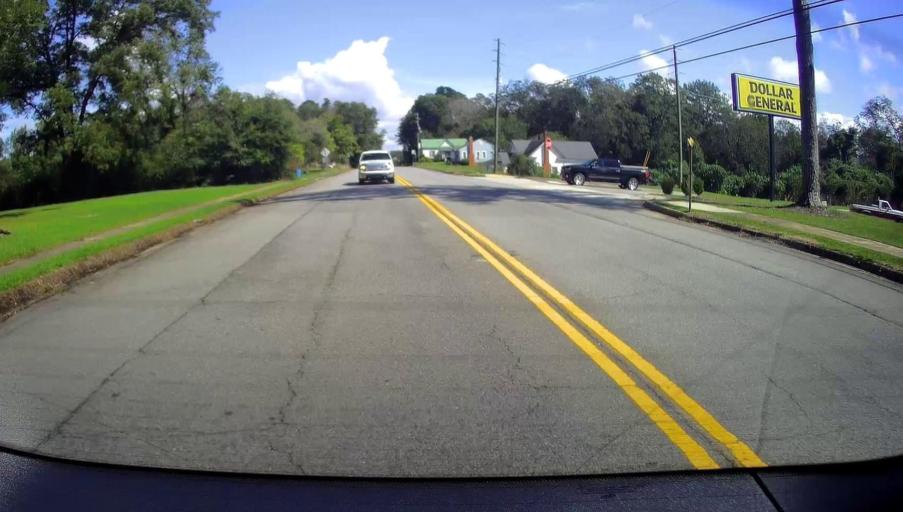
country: US
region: Georgia
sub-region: Jones County
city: Gray
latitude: 33.0329
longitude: -83.4278
